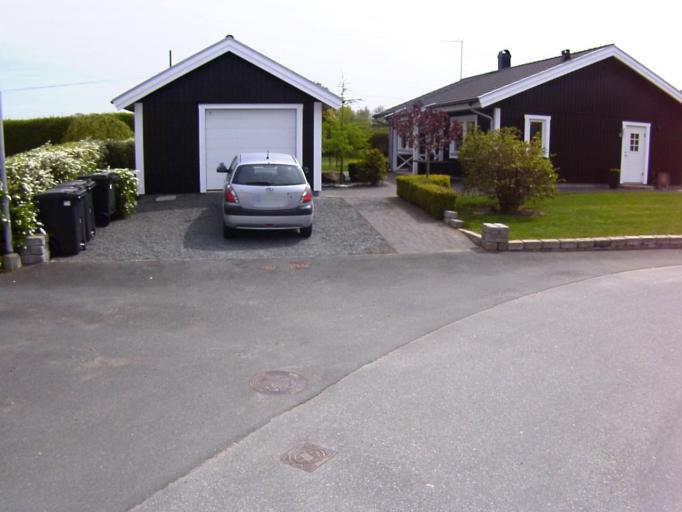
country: SE
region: Skane
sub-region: Kristianstads Kommun
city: Fjalkinge
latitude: 56.0791
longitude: 14.2170
